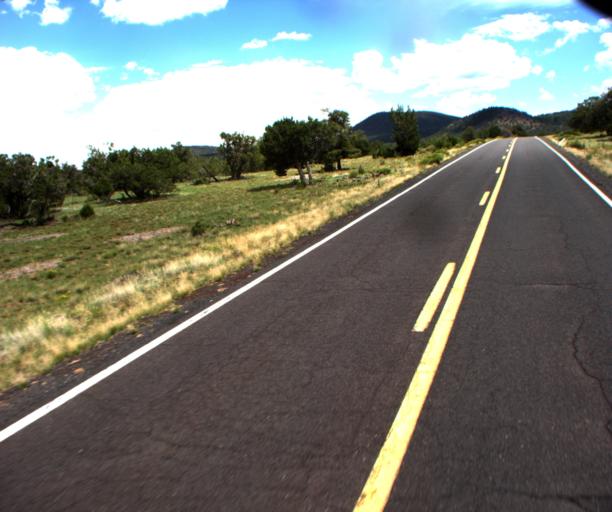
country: US
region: Arizona
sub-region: Coconino County
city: Parks
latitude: 35.5278
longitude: -111.8435
